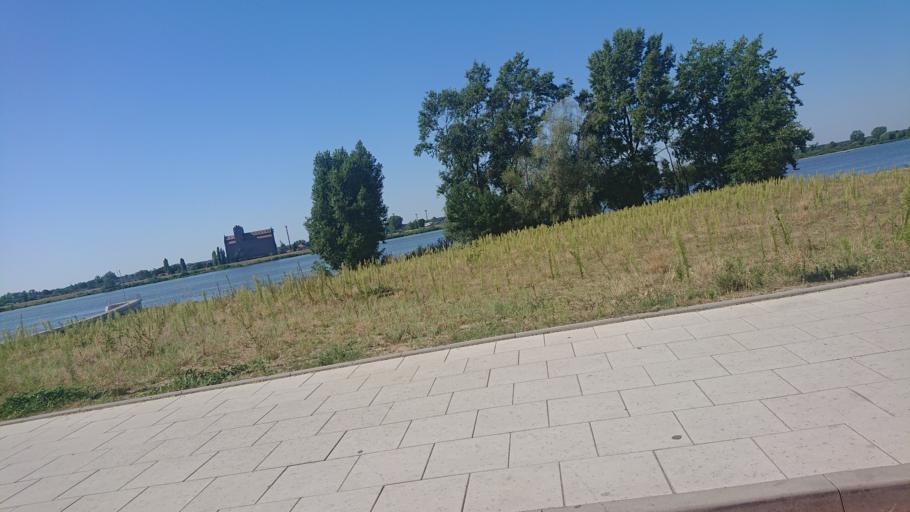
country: PL
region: Masovian Voivodeship
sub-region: Plock
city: Plock
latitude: 52.5423
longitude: 19.6840
